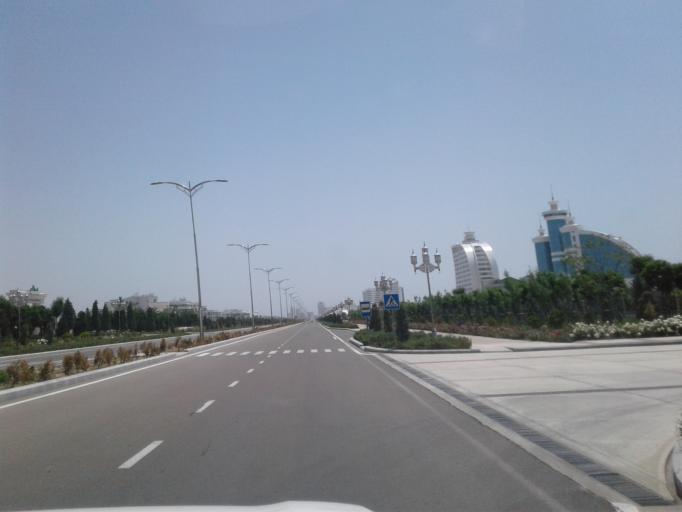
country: TM
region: Balkan
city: Turkmenbasy
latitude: 39.9851
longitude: 52.8251
